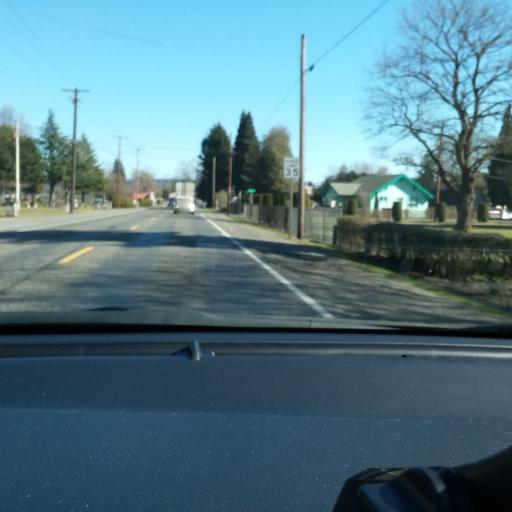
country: US
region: Washington
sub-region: Pierce County
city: North Puyallup
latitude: 47.2047
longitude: -122.2644
